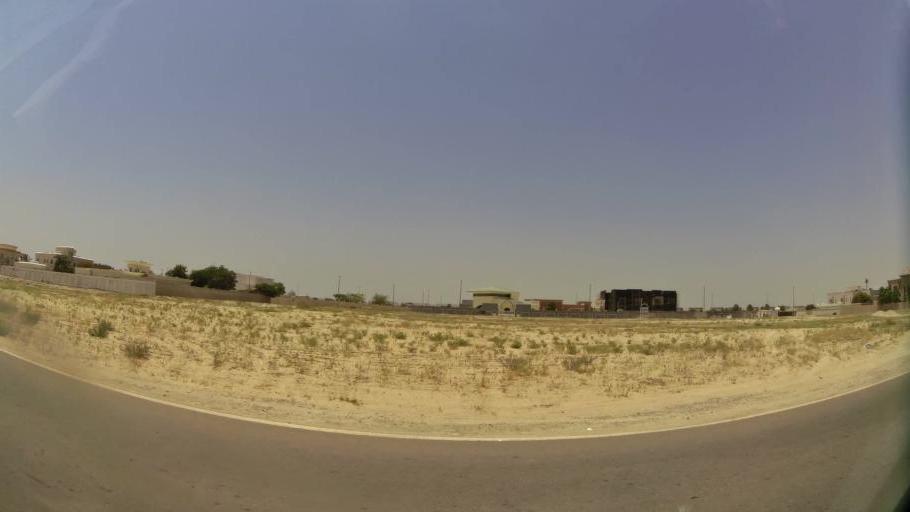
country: AE
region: Ajman
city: Ajman
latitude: 25.4212
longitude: 55.4946
